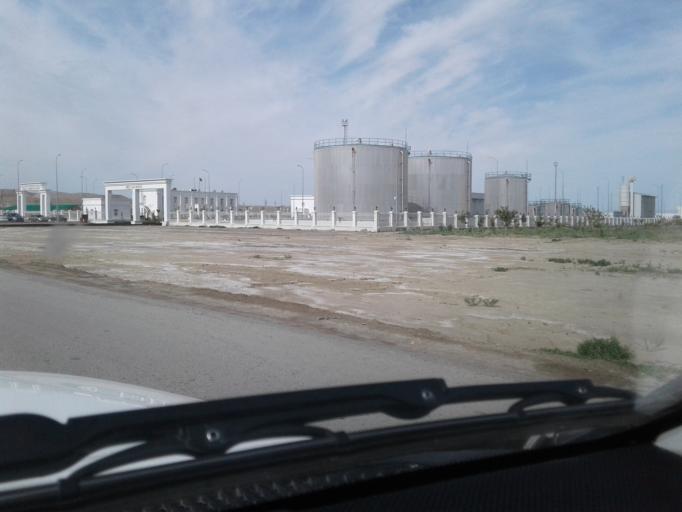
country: TM
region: Balkan
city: Gazanjyk
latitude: 39.2549
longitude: 55.4908
